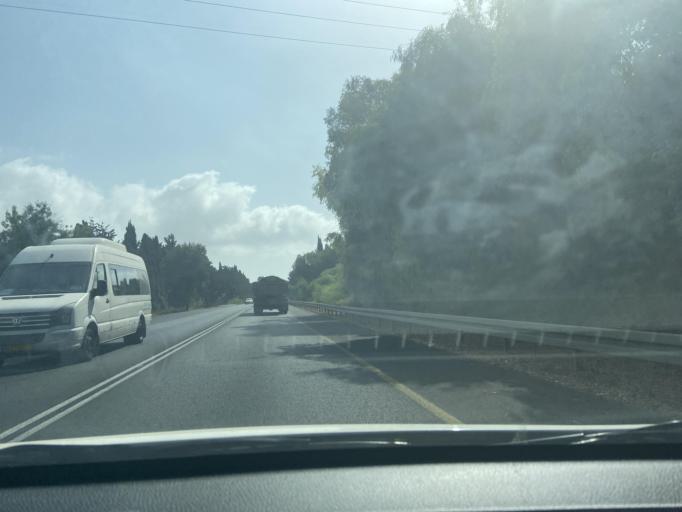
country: IL
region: Northern District
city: Nahariya
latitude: 33.0390
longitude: 35.1059
